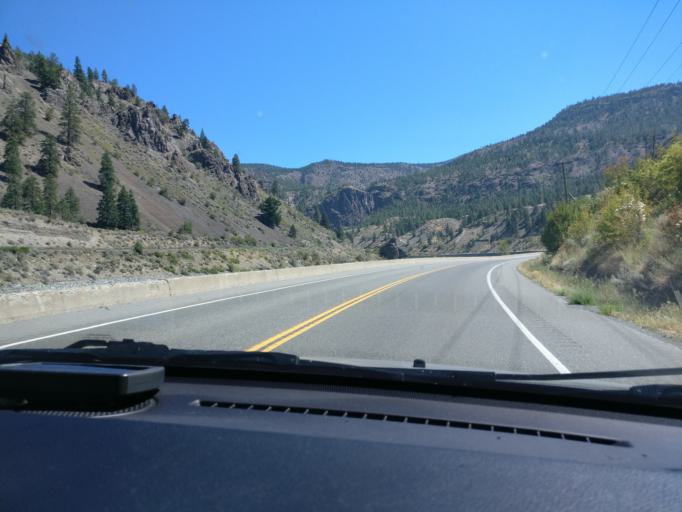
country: CA
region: British Columbia
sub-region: Thompson-Nicola Regional District
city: Ashcroft
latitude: 50.2631
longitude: -121.4156
